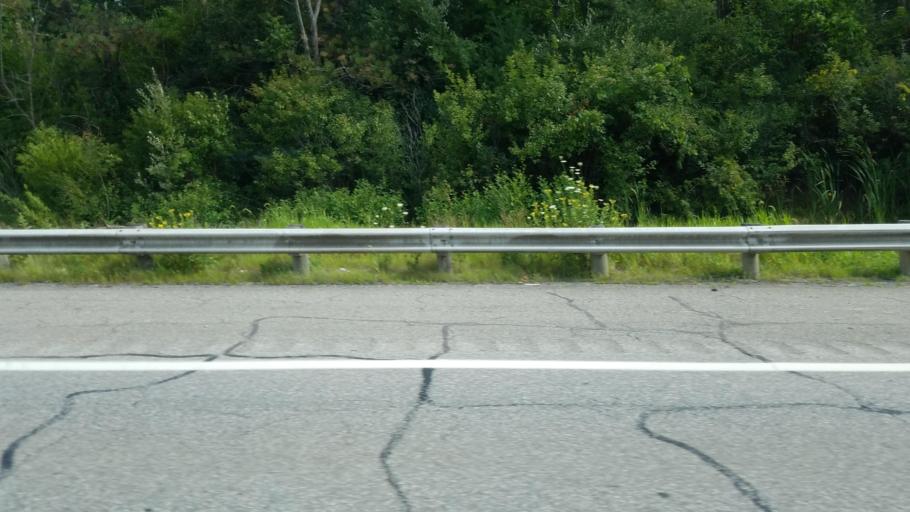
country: US
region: Ohio
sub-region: Trumbull County
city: Girard
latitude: 41.1239
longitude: -80.7273
